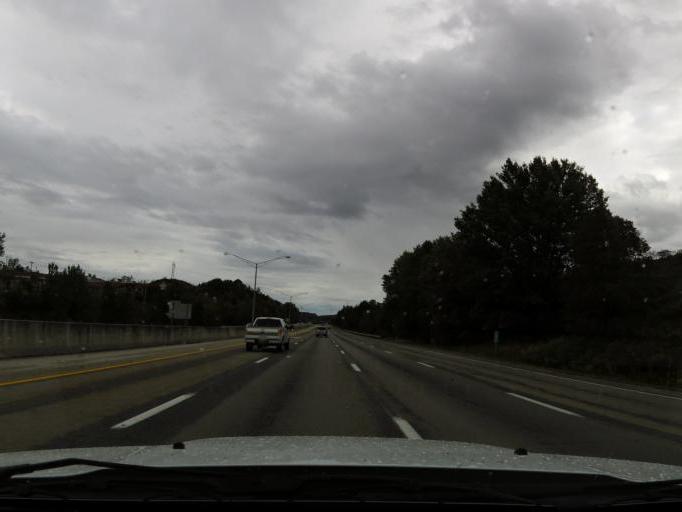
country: US
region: Kentucky
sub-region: Laurel County
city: London
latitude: 37.1498
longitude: -84.1116
